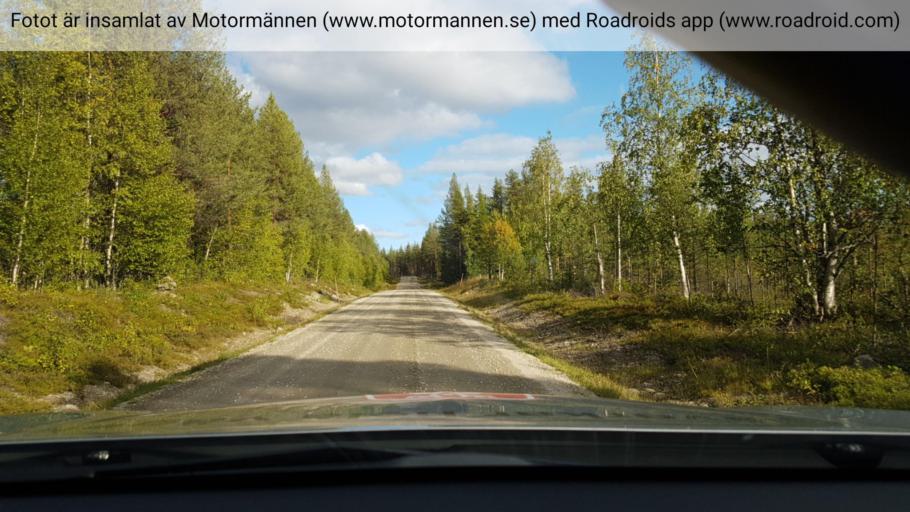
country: SE
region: Vaesterbotten
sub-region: Sorsele Kommun
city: Sorsele
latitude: 65.3615
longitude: 18.0297
